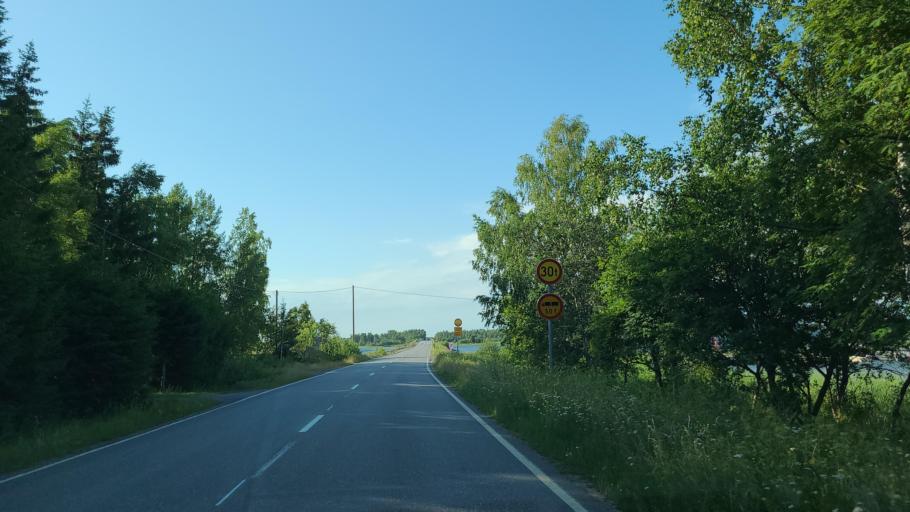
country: FI
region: Ostrobothnia
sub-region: Vaasa
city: Replot
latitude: 63.2705
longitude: 21.3459
